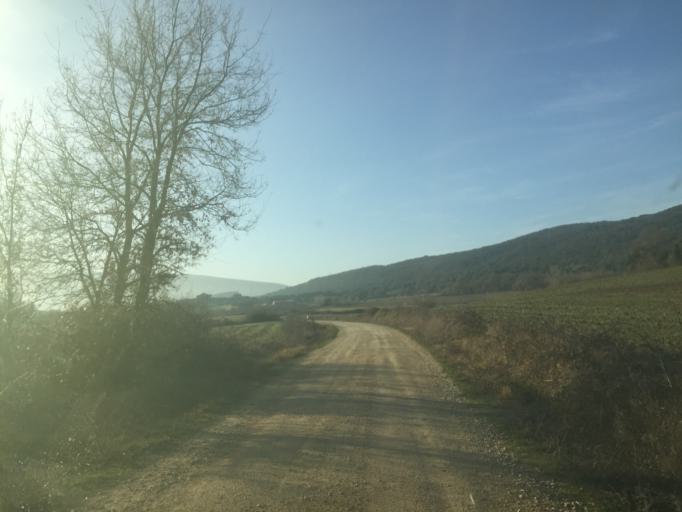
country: ES
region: Castille and Leon
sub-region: Provincia de Burgos
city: Medina de Pomar
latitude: 42.9321
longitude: -3.5939
